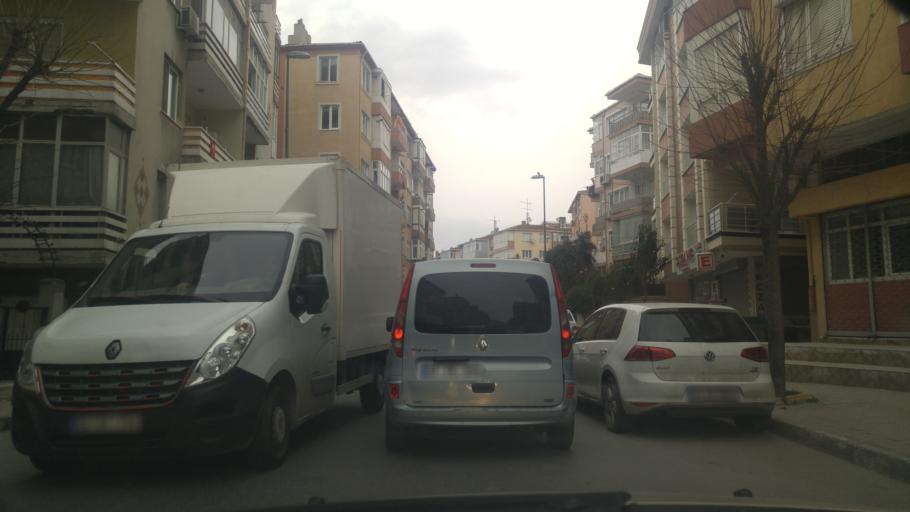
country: TR
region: Istanbul
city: Mahmutbey
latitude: 40.9983
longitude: 28.7663
